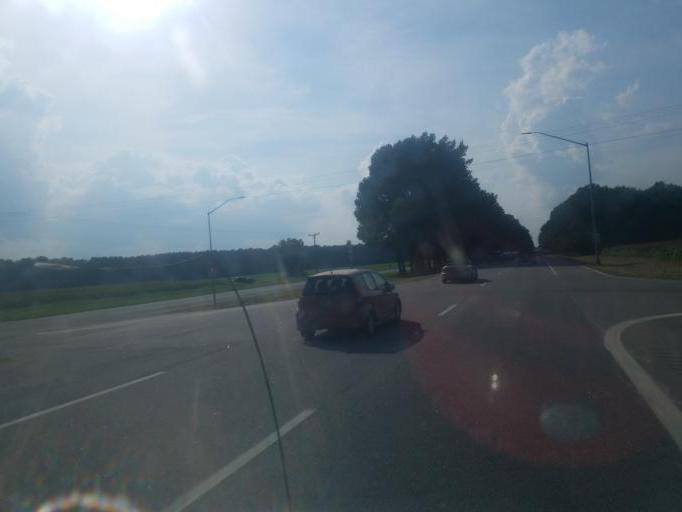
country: US
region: Maryland
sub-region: Worcester County
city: Berlin
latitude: 38.3562
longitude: -75.2463
